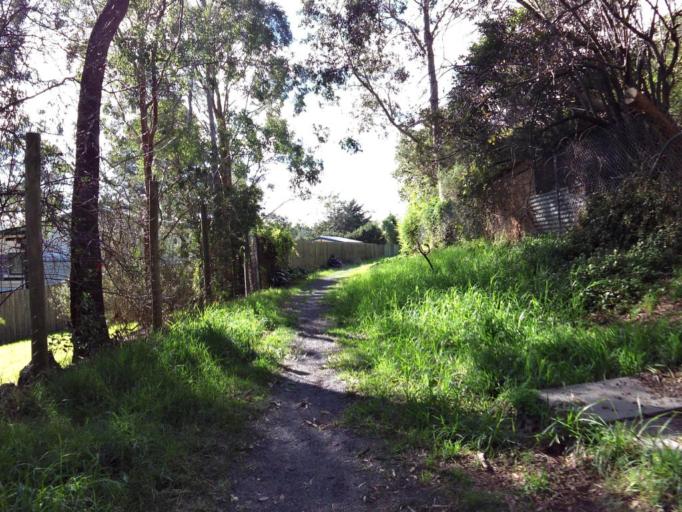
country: AU
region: Victoria
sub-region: Yarra Ranges
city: Mount Evelyn
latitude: -37.7823
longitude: 145.3661
